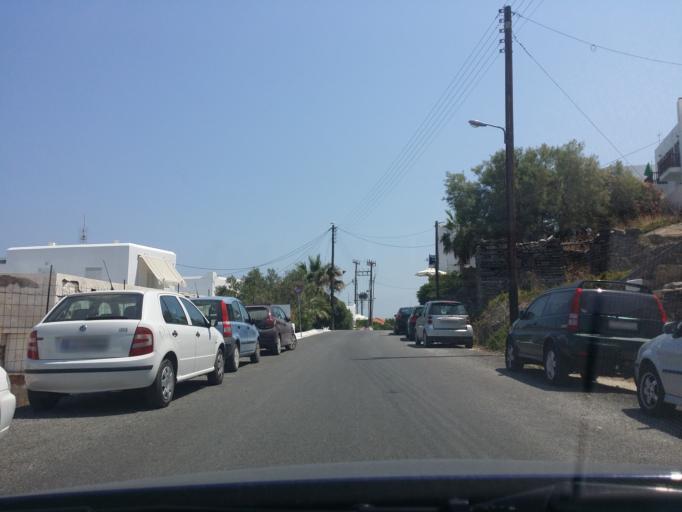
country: GR
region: South Aegean
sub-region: Nomos Kykladon
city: Naousa
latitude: 37.1228
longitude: 25.2343
